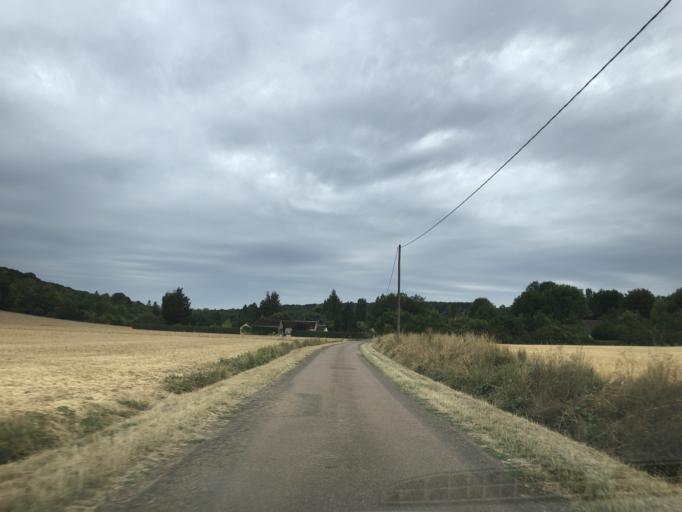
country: FR
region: Bourgogne
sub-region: Departement de l'Yonne
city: Aillant-sur-Tholon
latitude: 47.9041
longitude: 3.3311
